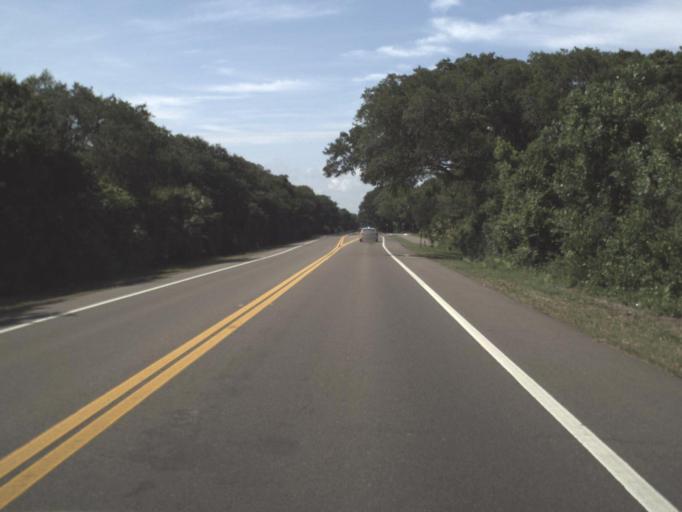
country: US
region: Florida
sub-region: Nassau County
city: Fernandina Beach
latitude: 30.5393
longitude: -81.4427
